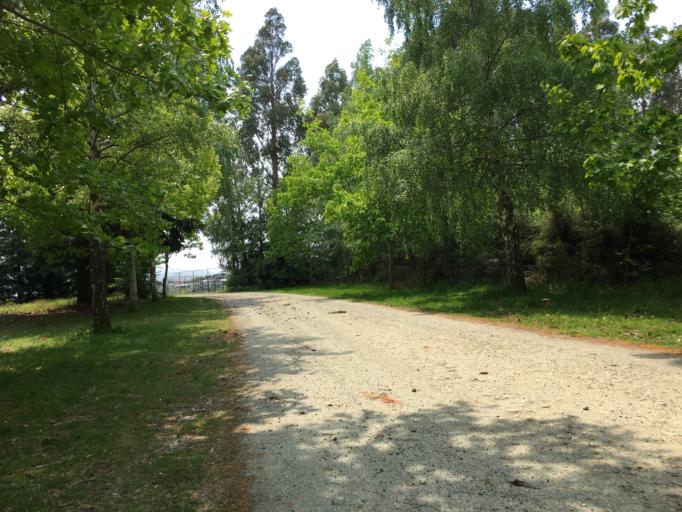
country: NZ
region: Otago
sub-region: Queenstown-Lakes District
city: Queenstown
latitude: -45.0464
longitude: 168.6910
